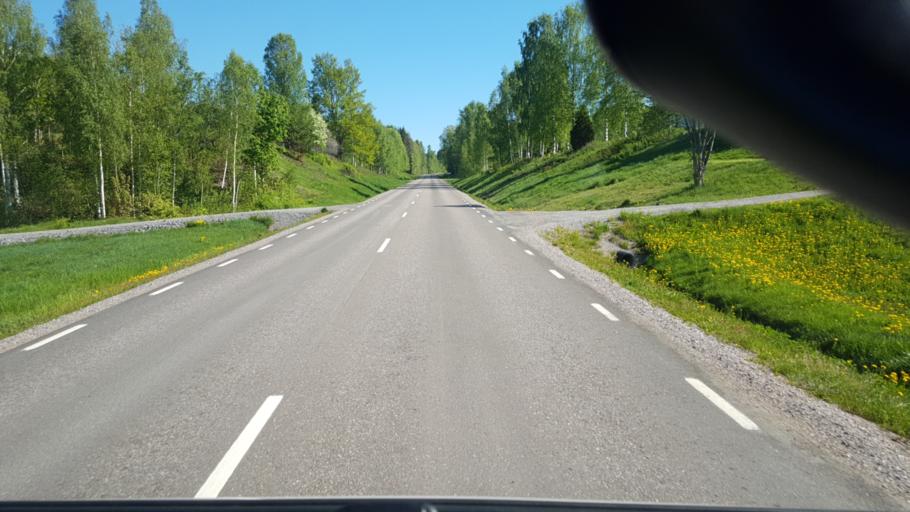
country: SE
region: Vaermland
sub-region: Eda Kommun
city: Amotfors
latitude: 59.6818
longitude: 12.4118
